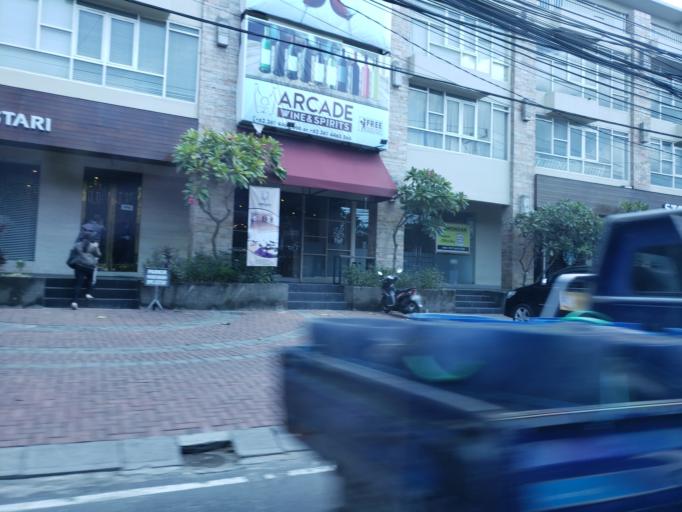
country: ID
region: Bali
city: Jimbaran
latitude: -8.7821
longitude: 115.1673
